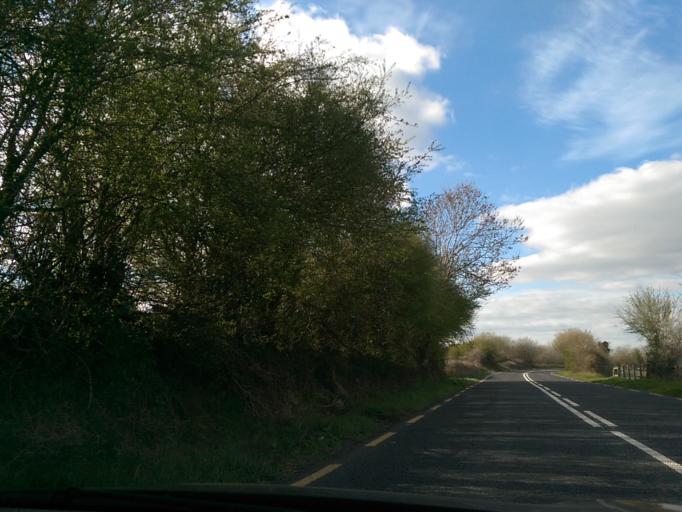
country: IE
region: Connaught
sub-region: County Galway
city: Portumna
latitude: 53.1276
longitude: -8.2450
